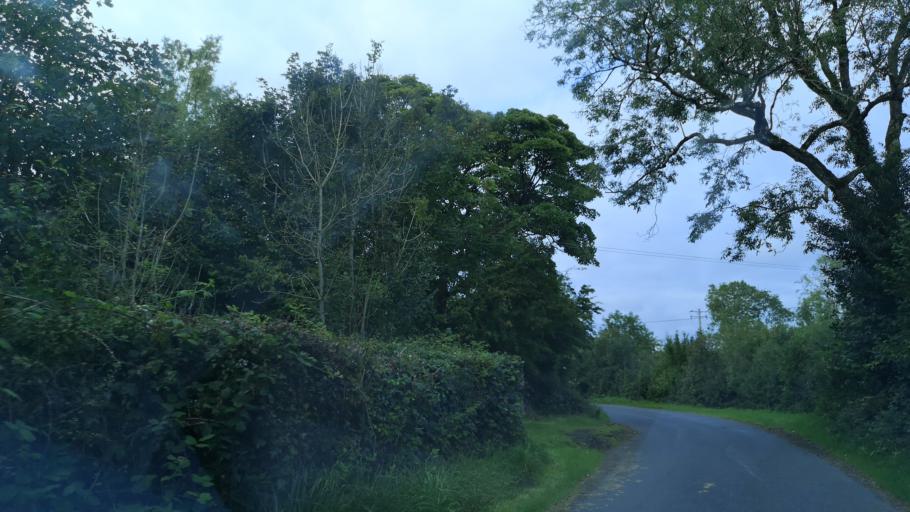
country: IE
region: Connaught
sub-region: County Galway
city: Ballinasloe
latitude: 53.3077
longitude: -8.0999
